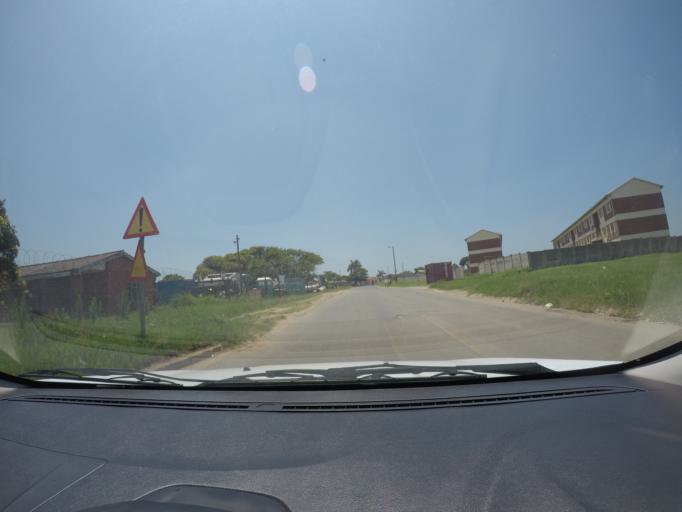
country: ZA
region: KwaZulu-Natal
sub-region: uThungulu District Municipality
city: eSikhawini
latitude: -28.8773
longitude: 31.9029
